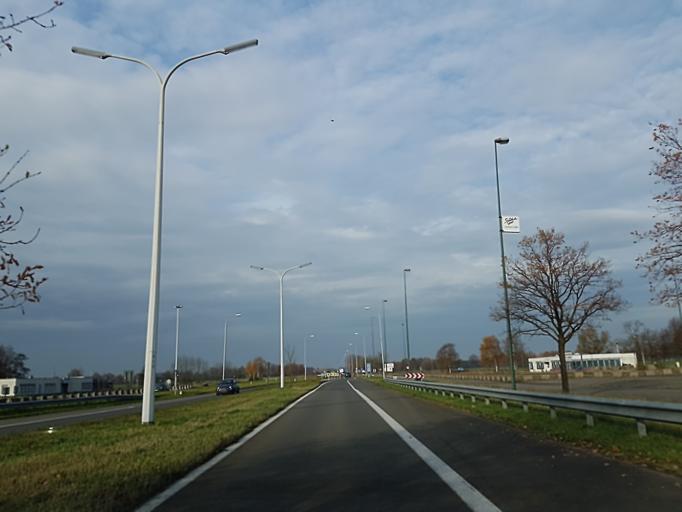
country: BE
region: Flanders
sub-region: Provincie Antwerpen
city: Essen
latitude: 51.4771
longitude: 4.4749
